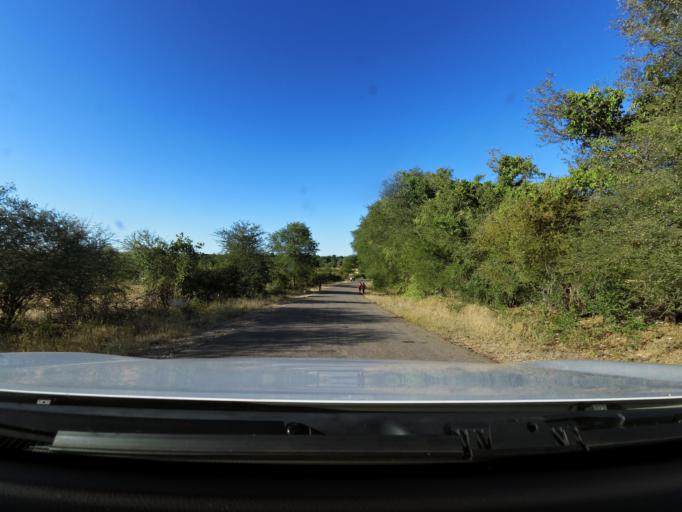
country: ZW
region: Matabeleland North
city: Kamativi Mine
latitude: -18.0094
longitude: 27.1420
